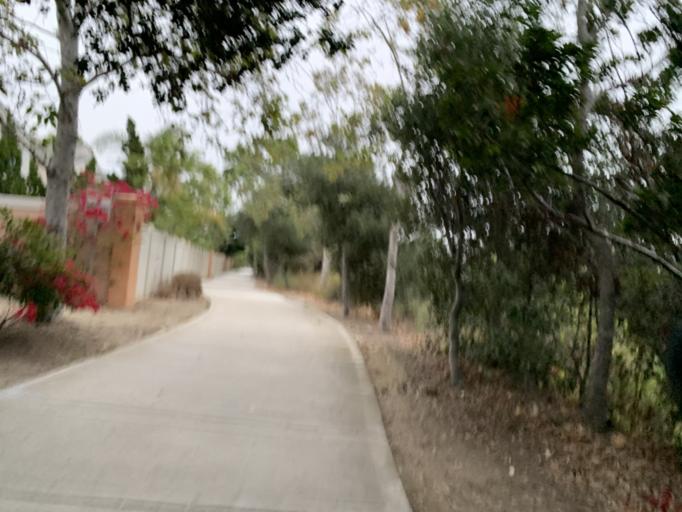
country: US
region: California
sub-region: San Diego County
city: San Diego
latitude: 32.7690
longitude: -117.1595
